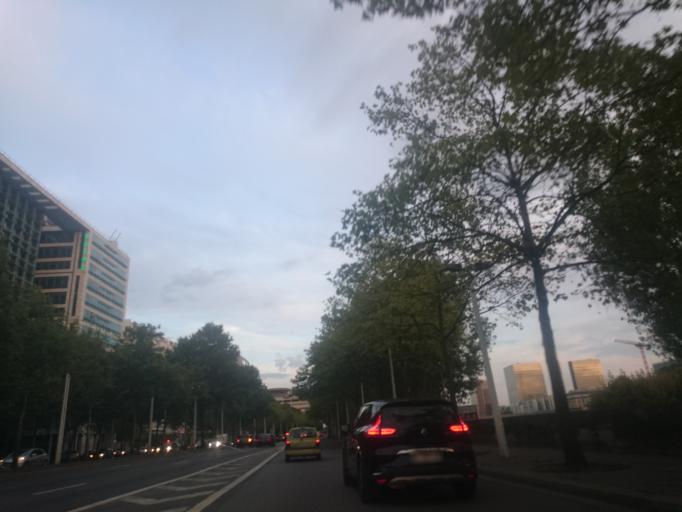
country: FR
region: Ile-de-France
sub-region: Paris
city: Paris
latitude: 48.8424
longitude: 2.3715
